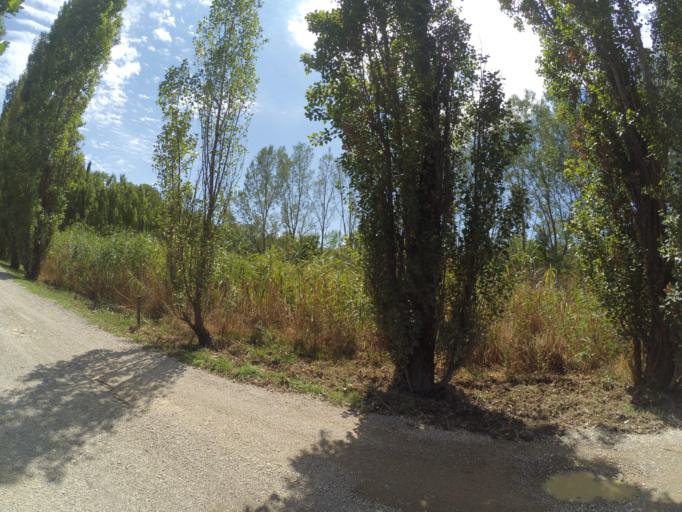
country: IT
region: Tuscany
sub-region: Province of Arezzo
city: Castiglion Fibocchi
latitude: 43.5295
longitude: 11.7778
